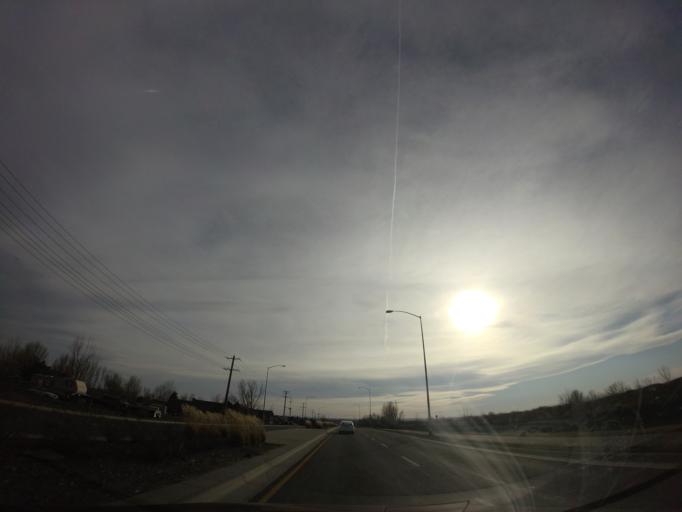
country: US
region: Montana
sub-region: Yellowstone County
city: Billings
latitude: 45.7444
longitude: -108.6175
